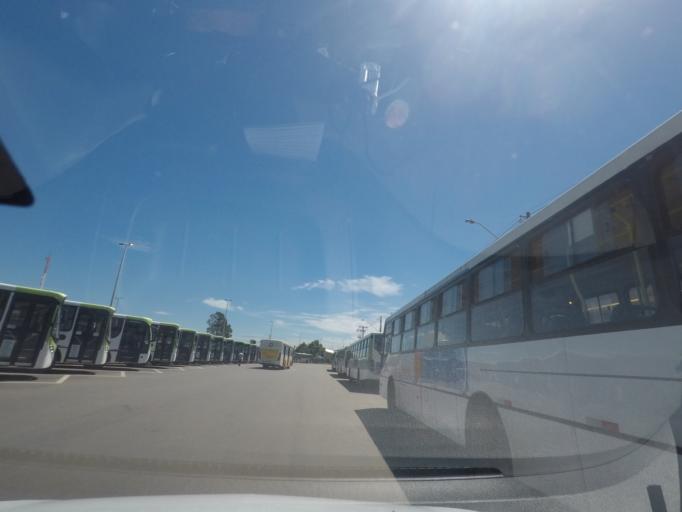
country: BR
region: Goias
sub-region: Aparecida De Goiania
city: Aparecida de Goiania
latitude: -16.7661
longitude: -49.3498
